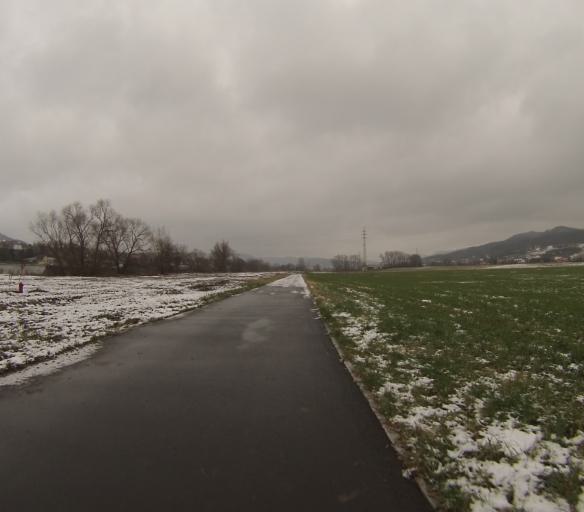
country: CZ
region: Ustecky
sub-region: Okres Decin
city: Decin
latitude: 50.7489
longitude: 14.1847
